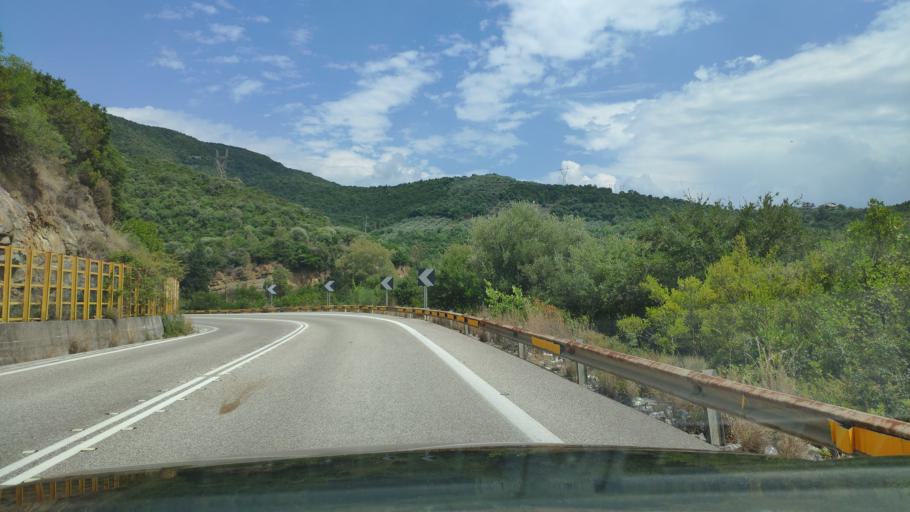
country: GR
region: West Greece
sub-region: Nomos Aitolias kai Akarnanias
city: Menidi
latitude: 39.0344
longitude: 21.1237
